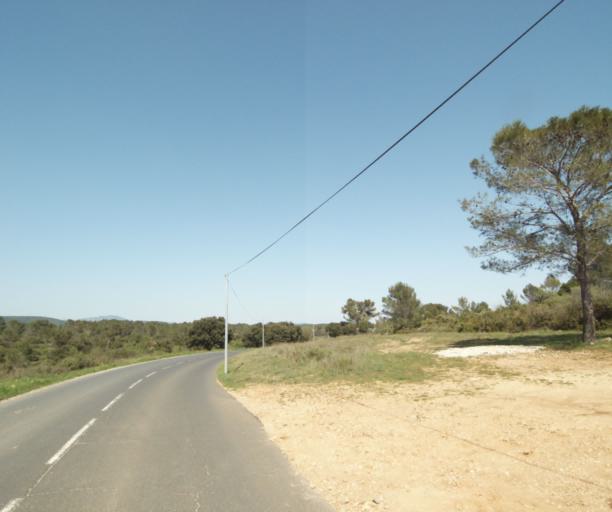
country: FR
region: Languedoc-Roussillon
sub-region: Departement de l'Herault
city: Combaillaux
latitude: 43.6401
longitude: 3.7499
